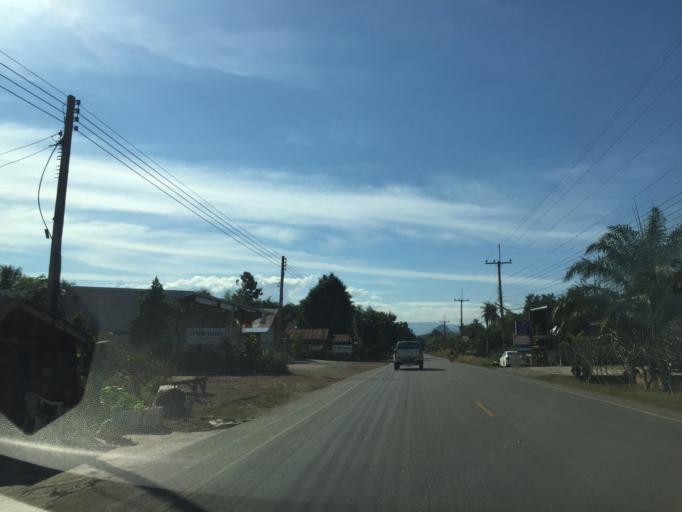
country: TH
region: Loei
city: Wang Saphung
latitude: 17.3154
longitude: 101.7497
